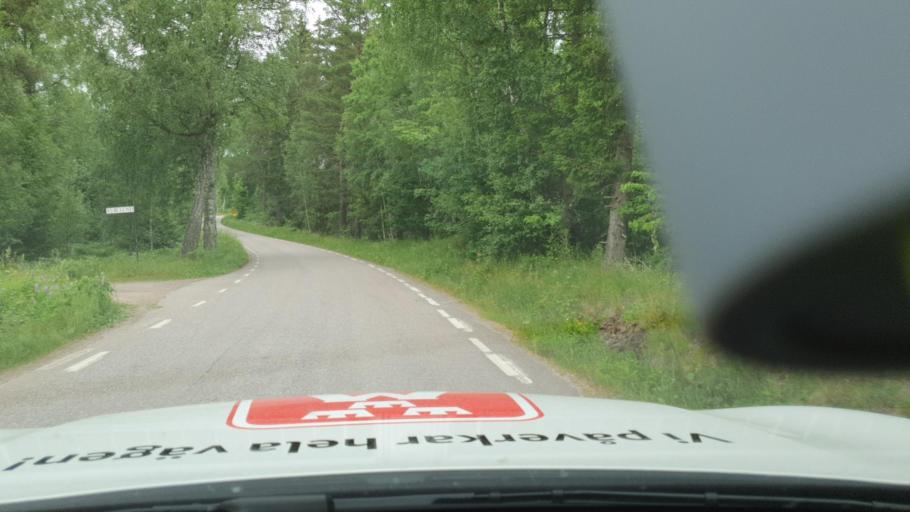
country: SE
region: Vaestra Goetaland
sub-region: Tibro Kommun
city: Tibro
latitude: 58.3485
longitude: 14.1570
